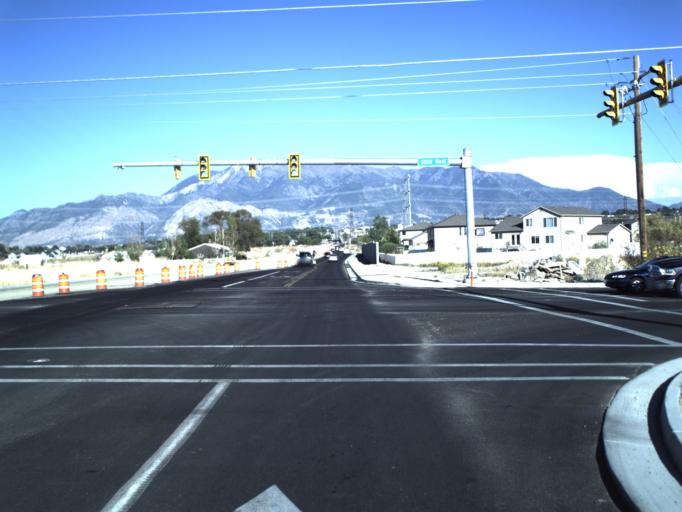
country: US
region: Utah
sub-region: Weber County
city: West Haven
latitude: 41.1906
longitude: -112.0647
